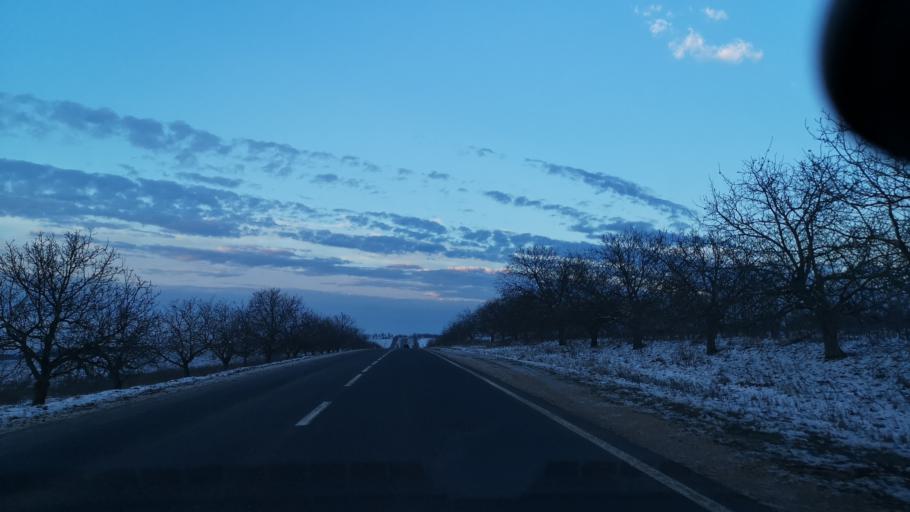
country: MD
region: Rezina
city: Saharna
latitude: 47.6155
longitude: 28.8319
